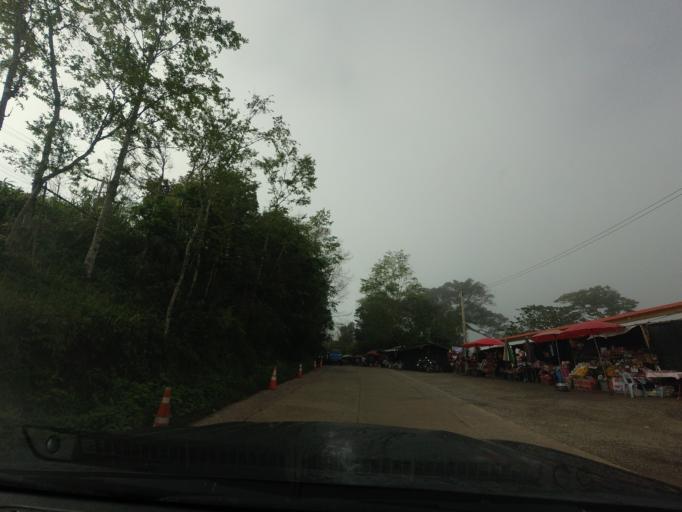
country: TH
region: Phetchabun
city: Lom Kao
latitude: 16.9004
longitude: 101.1044
